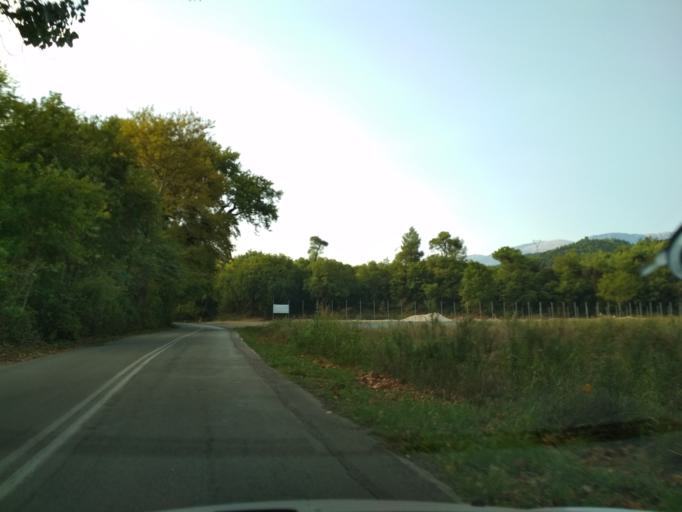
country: GR
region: Central Greece
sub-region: Nomos Evvoias
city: Mantoudi
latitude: 38.7722
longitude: 23.4757
